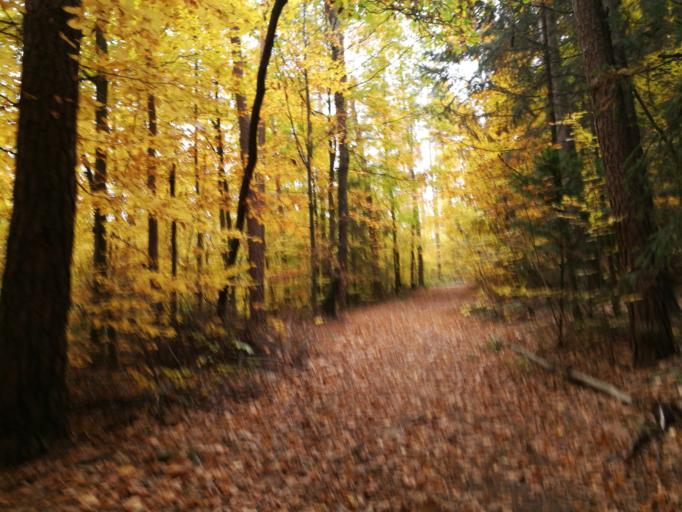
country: DE
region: Bavaria
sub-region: Regierungsbezirk Mittelfranken
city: Zirndorf
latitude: 49.4678
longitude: 10.9361
